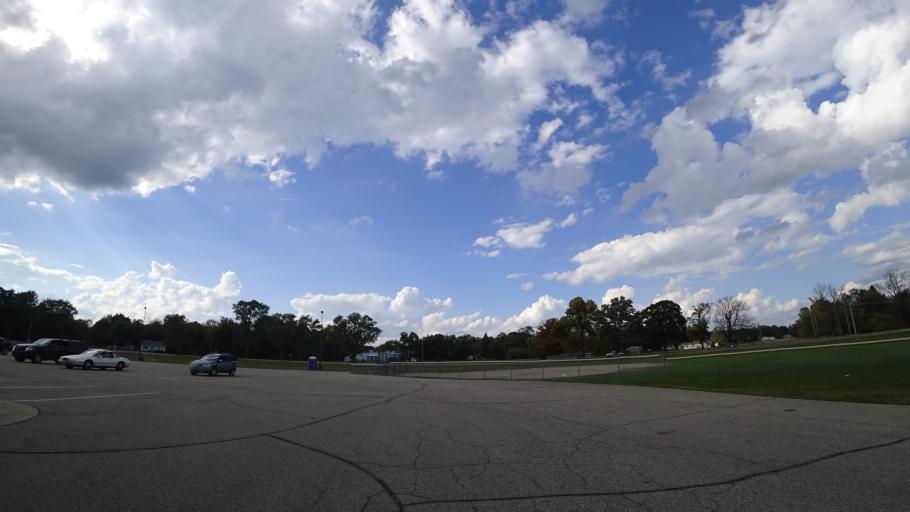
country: US
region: Michigan
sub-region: Saint Joseph County
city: Three Rivers
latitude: 41.9534
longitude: -85.6175
